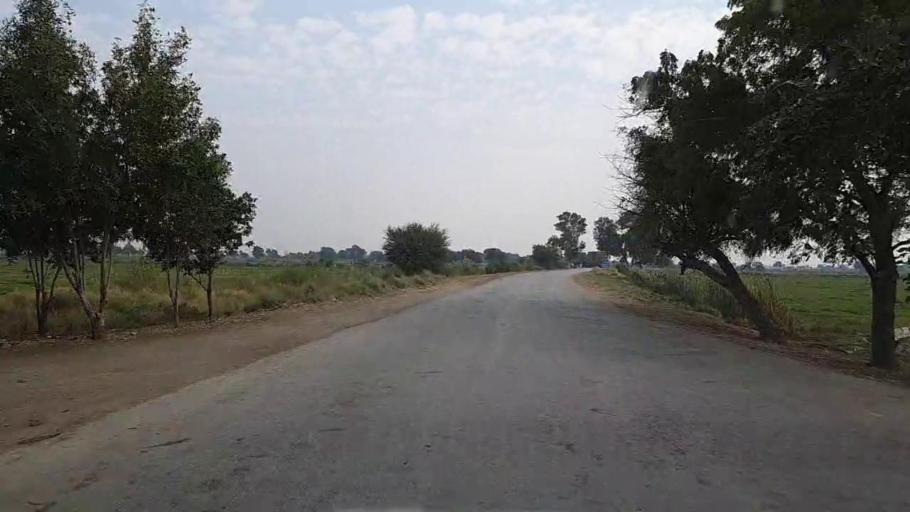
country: PK
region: Sindh
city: Mirwah Gorchani
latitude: 25.3971
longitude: 69.0697
